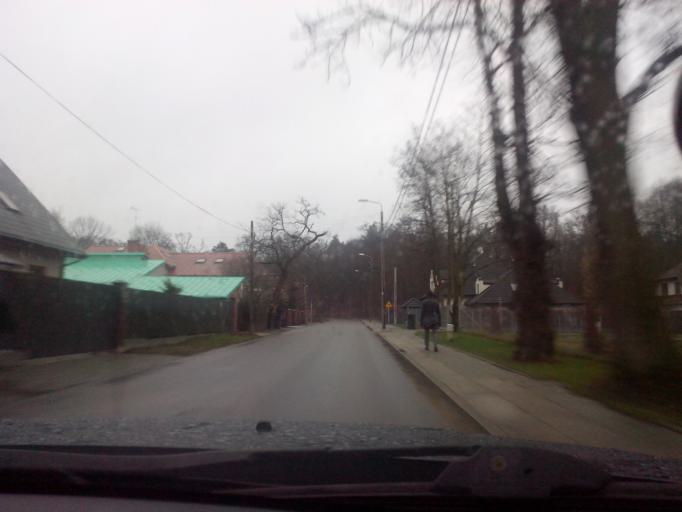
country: PL
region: Masovian Voivodeship
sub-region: Warszawa
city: Bialoleka
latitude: 52.3403
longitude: 20.9785
